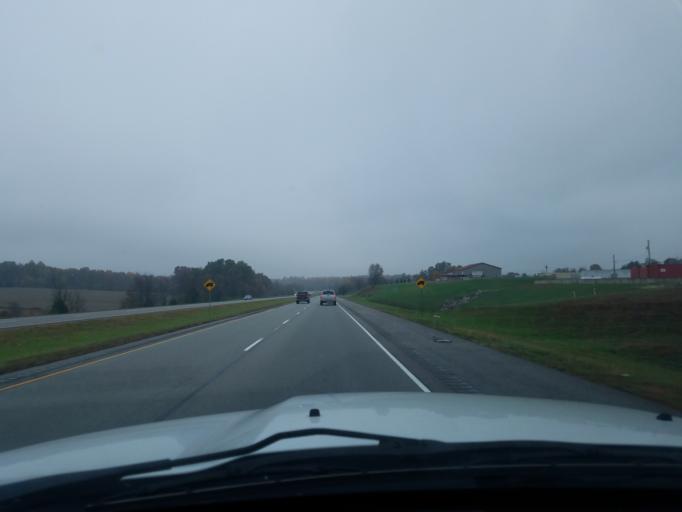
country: US
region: Kentucky
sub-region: Hardin County
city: Elizabethtown
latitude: 37.6511
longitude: -85.8373
